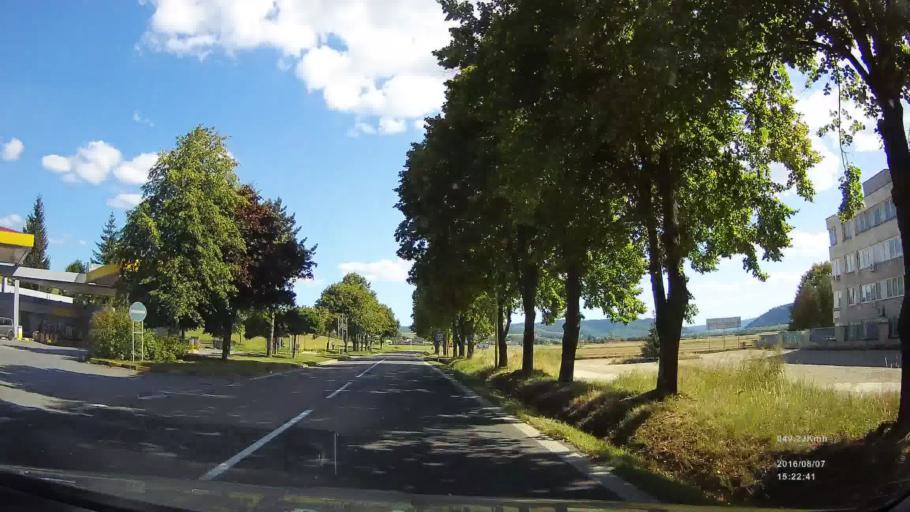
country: SK
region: Presovsky
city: Stropkov
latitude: 49.1908
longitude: 21.6571
